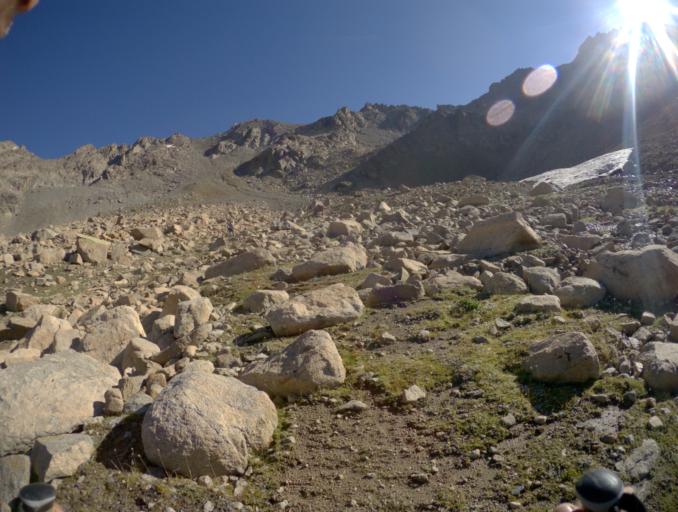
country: RU
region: Kabardino-Balkariya
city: Terskol
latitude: 43.3249
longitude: 42.5317
